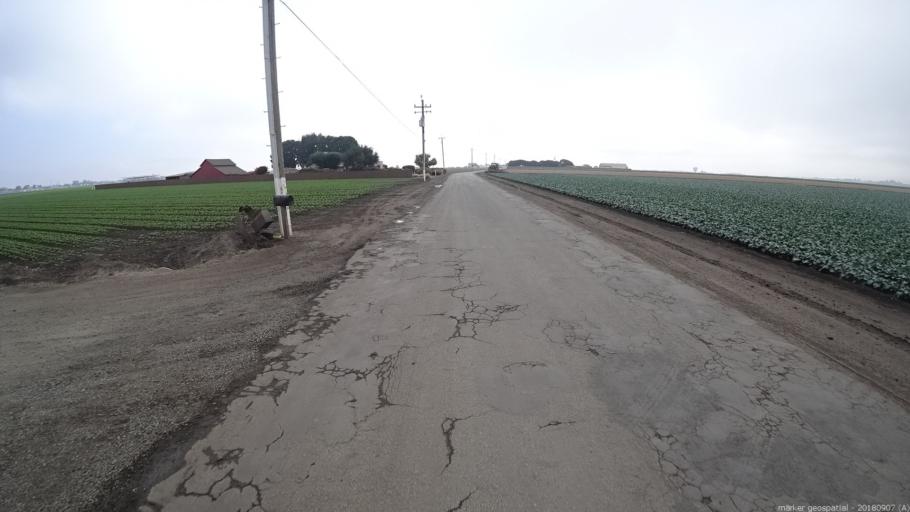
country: US
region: California
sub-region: Monterey County
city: Salinas
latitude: 36.6450
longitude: -121.6537
